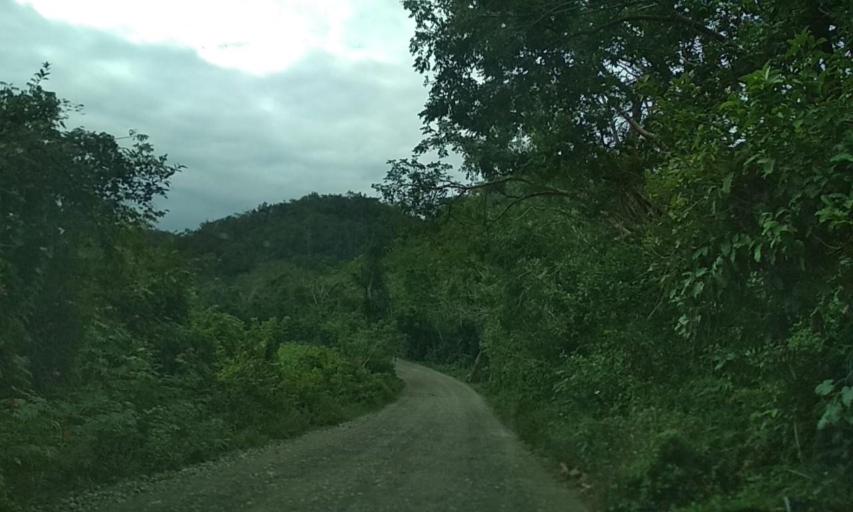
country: MX
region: Veracruz
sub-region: Papantla
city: Residencial Tajin
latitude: 20.6247
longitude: -97.3637
